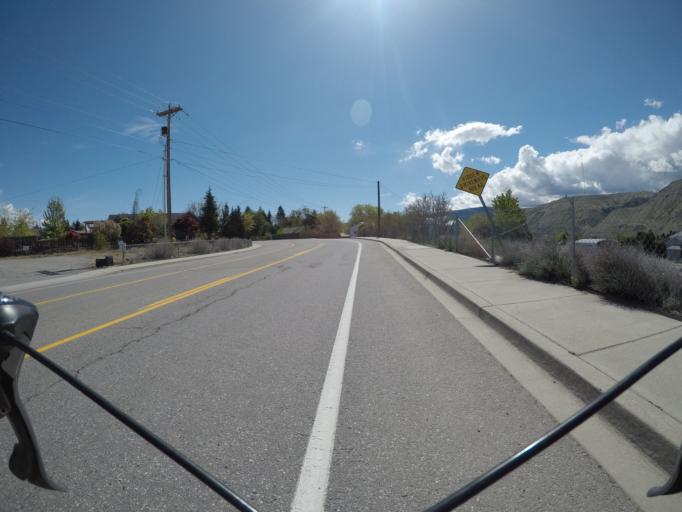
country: US
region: Washington
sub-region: Chelan County
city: South Wenatchee
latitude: 47.3990
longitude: -120.2747
